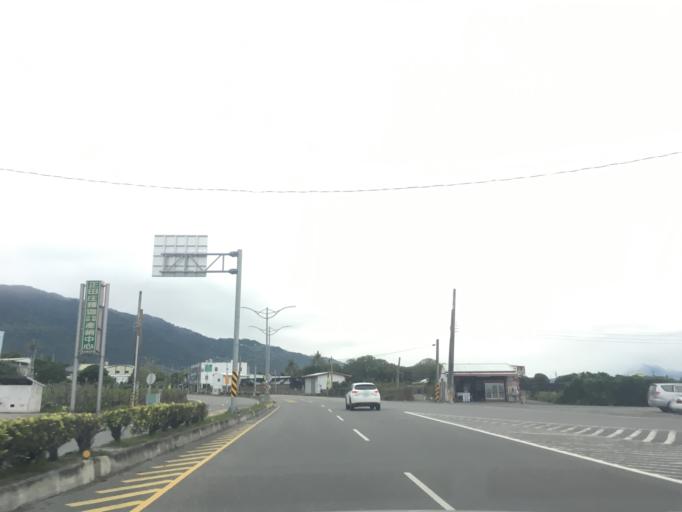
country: TW
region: Taiwan
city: Taitung City
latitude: 22.6909
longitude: 121.0465
